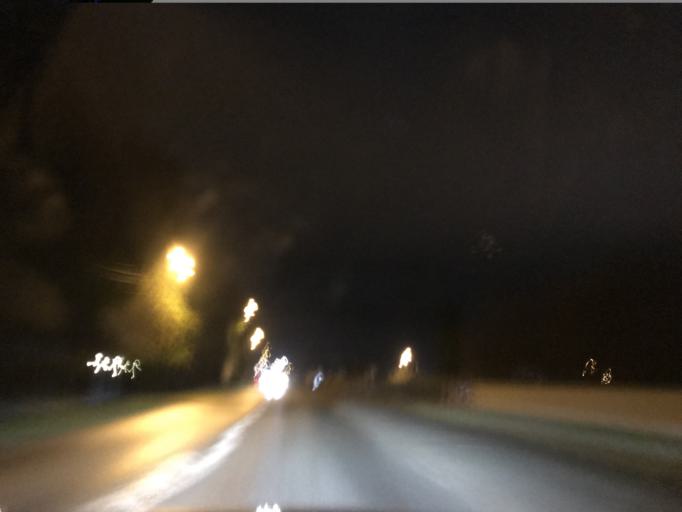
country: FR
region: Auvergne
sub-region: Departement de l'Allier
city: Hauterive
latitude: 46.0926
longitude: 3.4401
